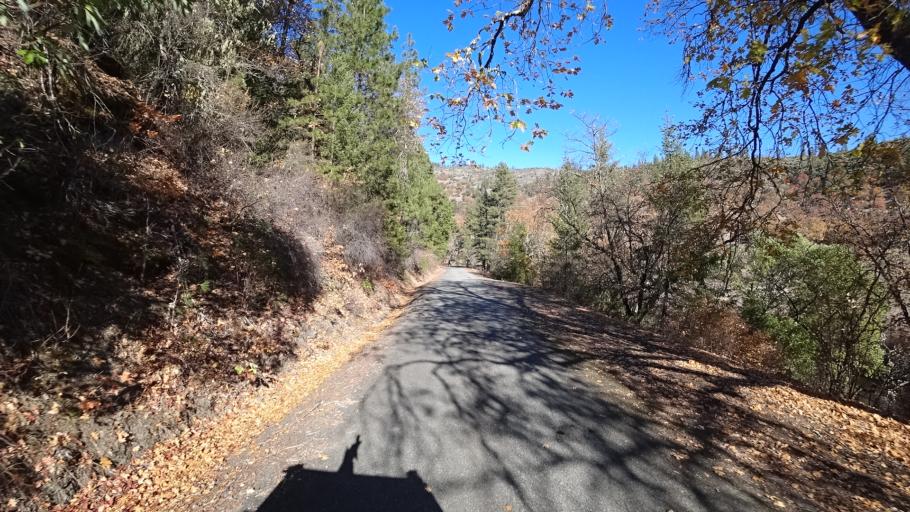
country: US
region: California
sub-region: Siskiyou County
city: Yreka
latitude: 41.8435
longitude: -122.9003
